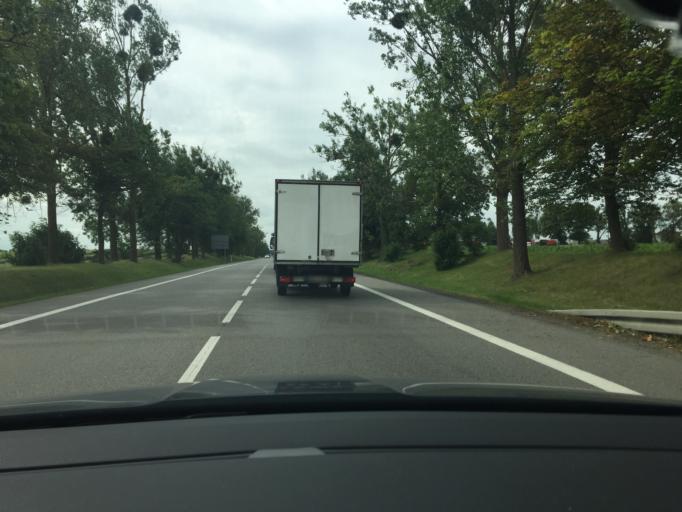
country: PL
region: Pomeranian Voivodeship
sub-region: Powiat tczewski
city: Subkowy
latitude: 54.0458
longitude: 18.7608
